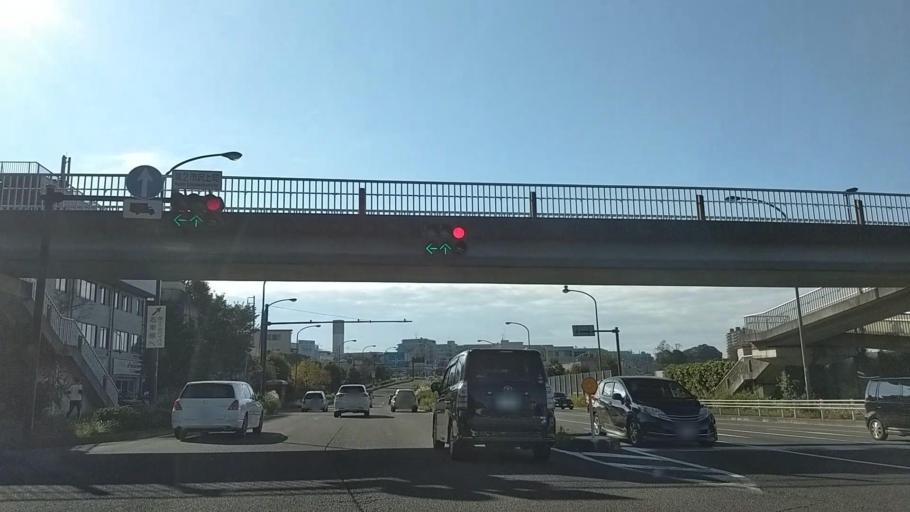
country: JP
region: Kanagawa
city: Yokohama
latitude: 35.4574
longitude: 139.5631
